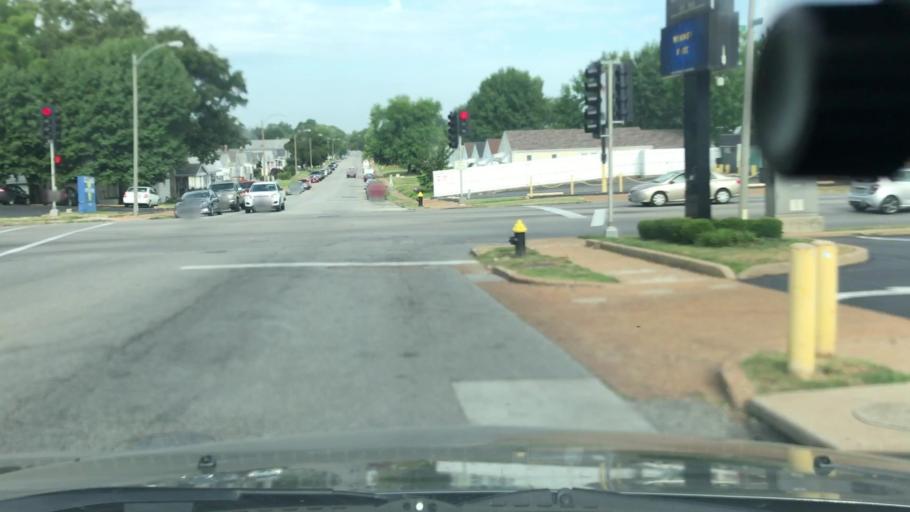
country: US
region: Missouri
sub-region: Saint Louis County
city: Maplewood
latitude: 38.6020
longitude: -90.2916
